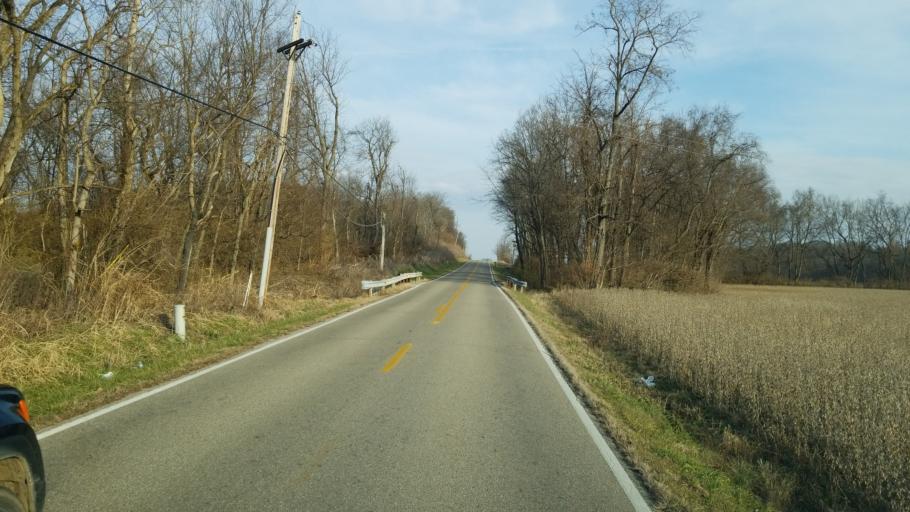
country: US
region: Ohio
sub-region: Ross County
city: Kingston
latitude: 39.4099
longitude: -82.9412
